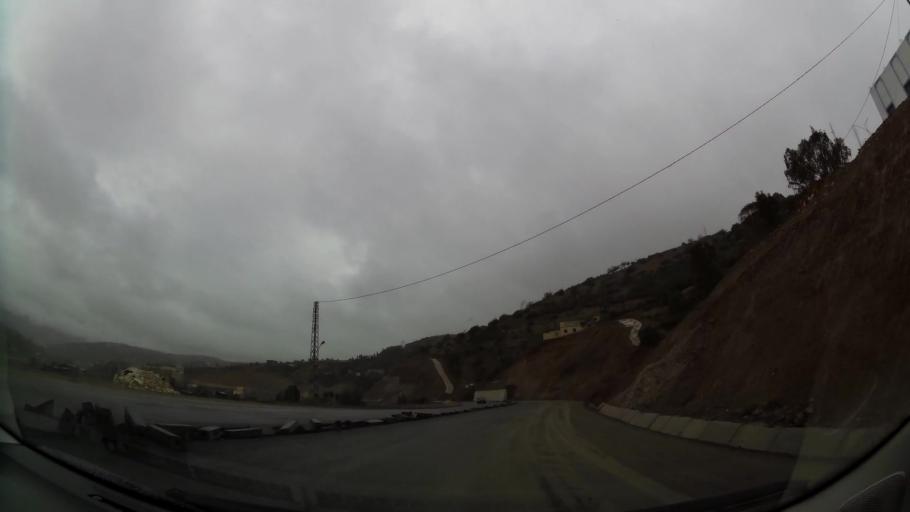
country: MA
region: Taza-Al Hoceima-Taounate
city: Imzourene
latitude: 35.0283
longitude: -3.8209
